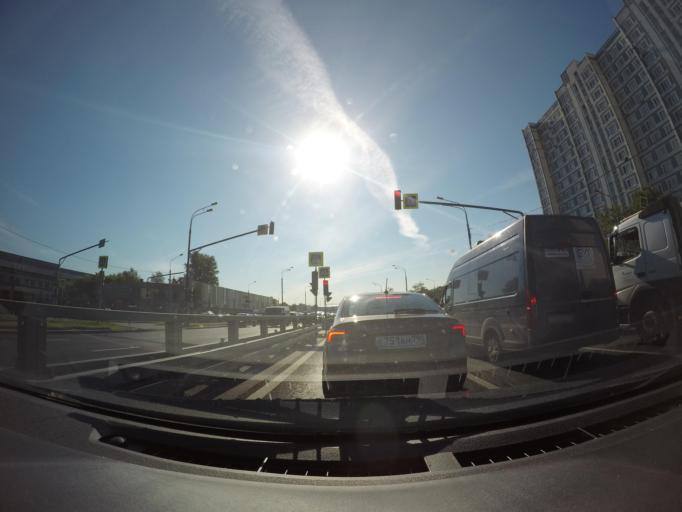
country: RU
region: Moscow
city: Vykhino-Zhulebino
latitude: 55.7126
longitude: 37.8148
